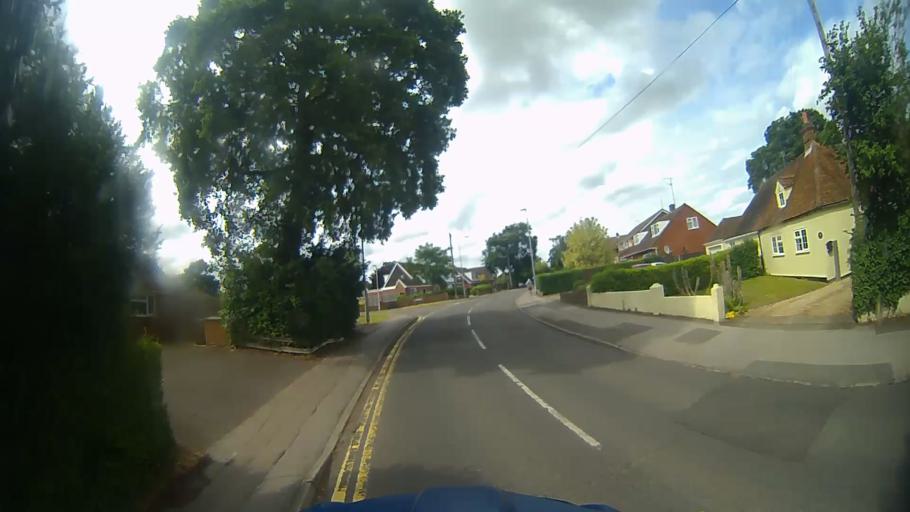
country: GB
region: England
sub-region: Wokingham
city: Earley
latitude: 51.4497
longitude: -0.9064
